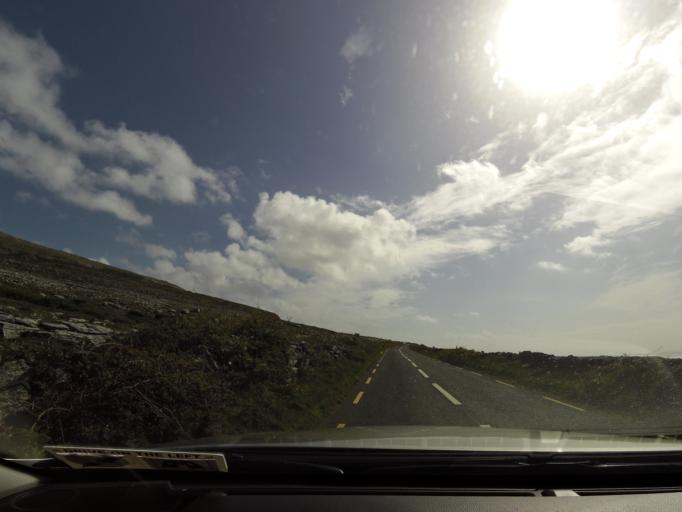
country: IE
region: Connaught
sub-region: County Galway
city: Bearna
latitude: 53.1458
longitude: -9.2722
